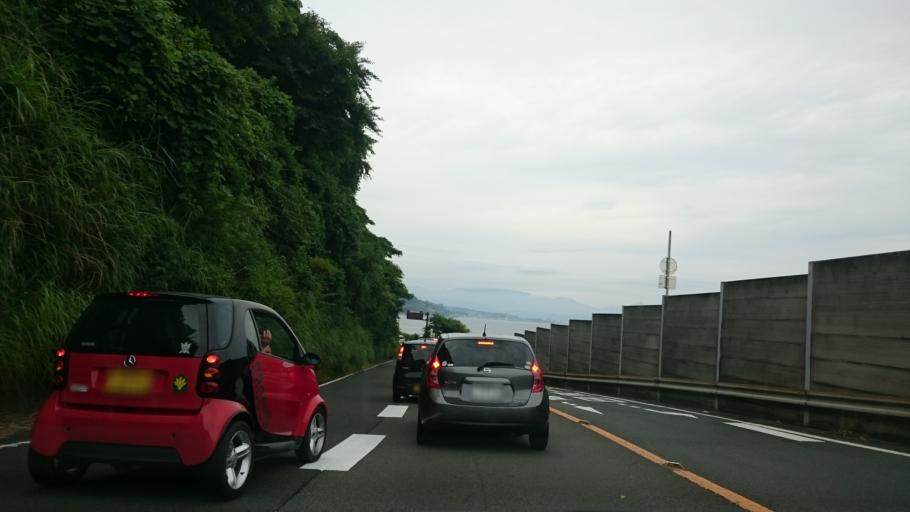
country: JP
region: Kanagawa
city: Yugawara
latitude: 35.1714
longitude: 139.1430
